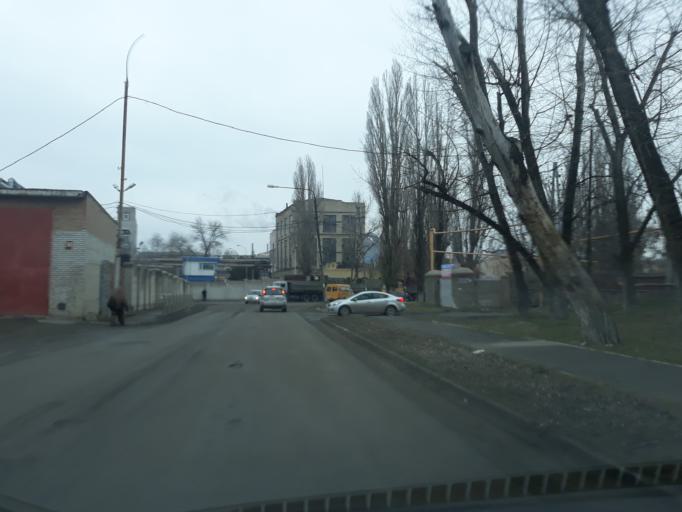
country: RU
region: Rostov
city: Taganrog
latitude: 47.2377
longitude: 38.9272
